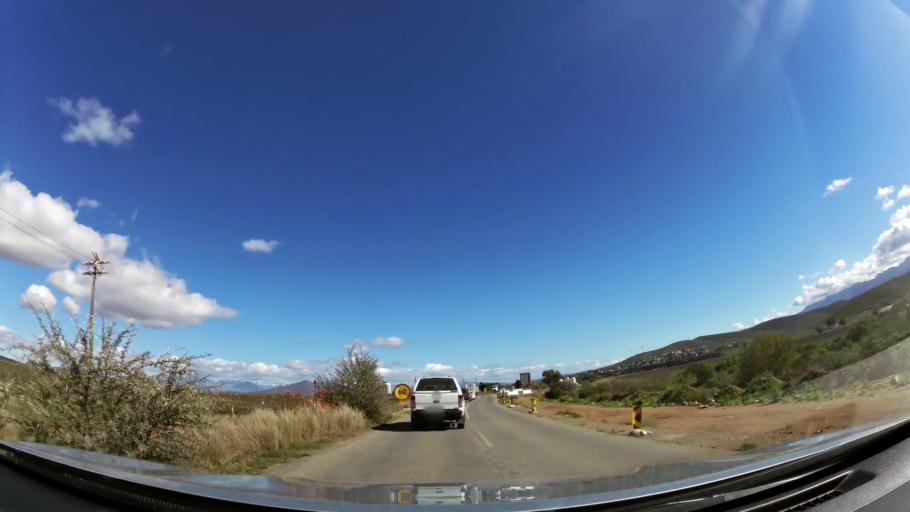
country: ZA
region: Western Cape
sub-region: Cape Winelands District Municipality
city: Ashton
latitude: -33.8304
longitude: 20.0823
